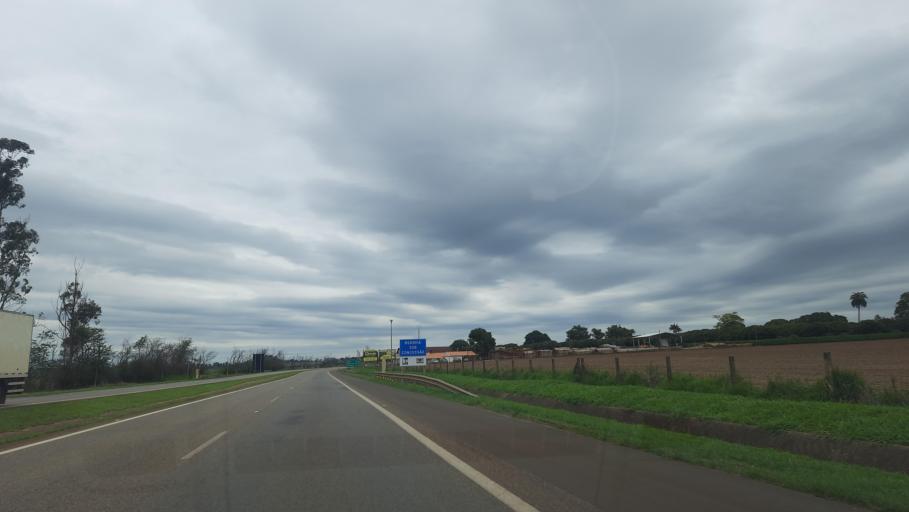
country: BR
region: Sao Paulo
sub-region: Casa Branca
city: Casa Branca
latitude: -21.7926
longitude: -47.0619
